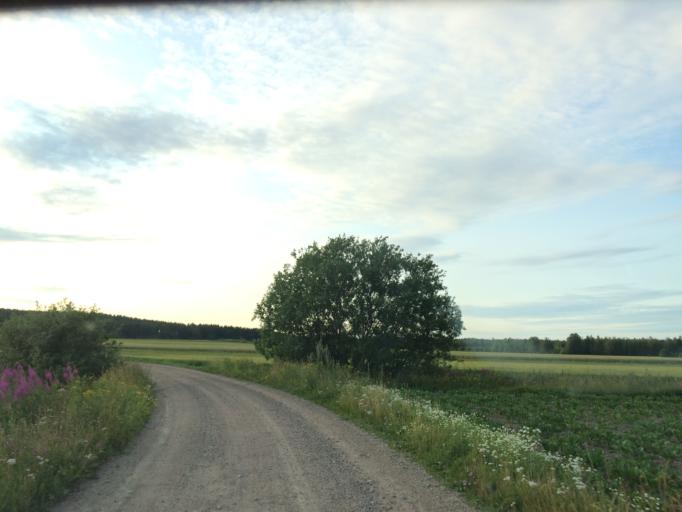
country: FI
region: Haeme
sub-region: Haemeenlinna
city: Turenki
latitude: 60.8845
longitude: 24.6327
